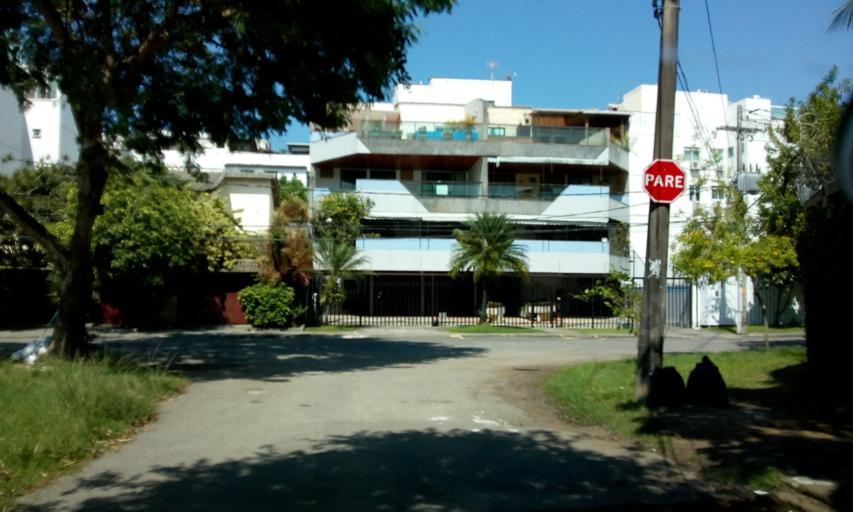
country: BR
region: Rio de Janeiro
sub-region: Nilopolis
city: Nilopolis
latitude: -23.0165
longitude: -43.4618
